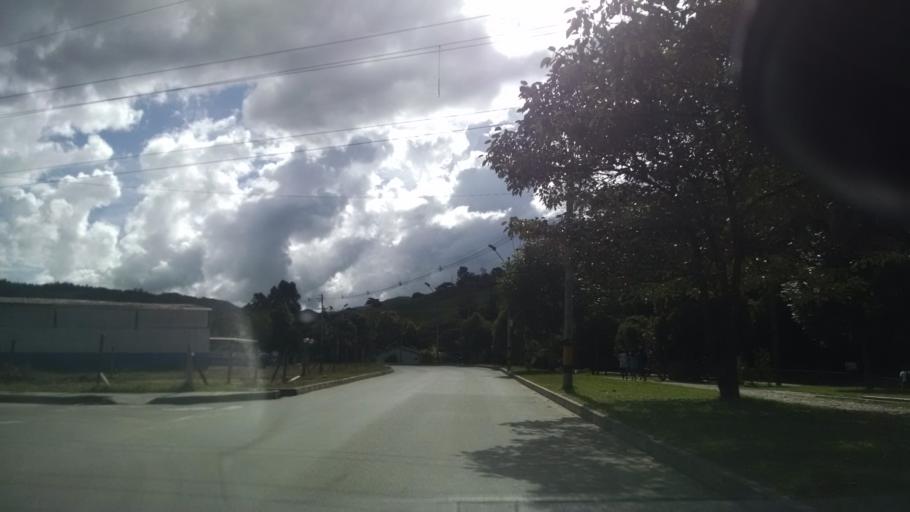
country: CO
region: Antioquia
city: El Retiro
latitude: 6.0617
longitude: -75.5035
